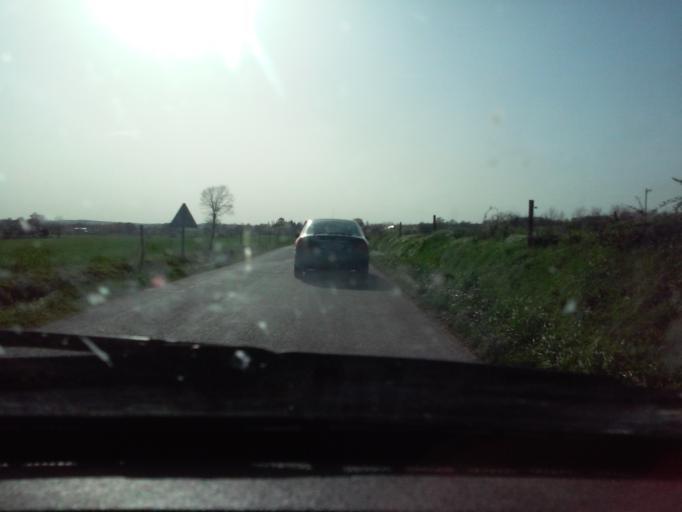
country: FR
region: Brittany
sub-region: Departement d'Ille-et-Vilaine
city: Saint-Sauveur-des-Landes
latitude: 48.3002
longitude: -1.3212
